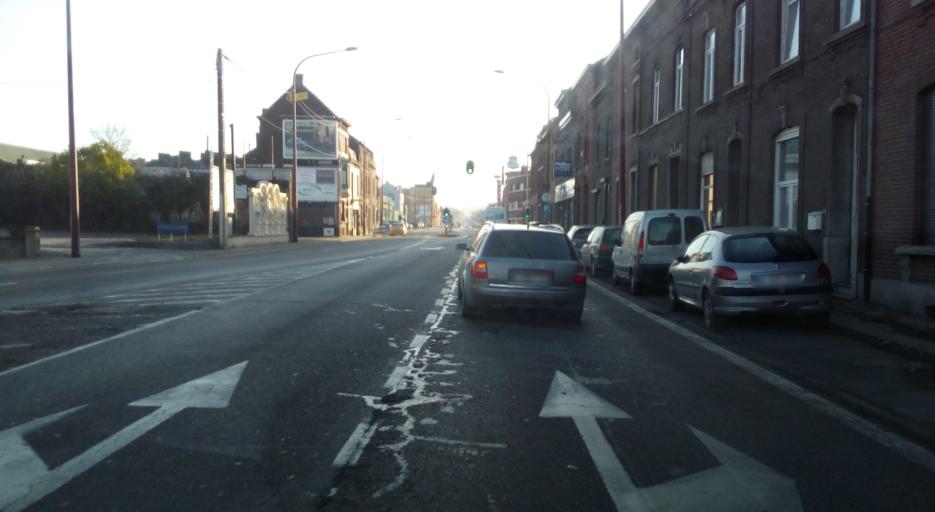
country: BE
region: Wallonia
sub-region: Province du Hainaut
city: Charleroi
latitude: 50.4003
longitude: 4.4526
